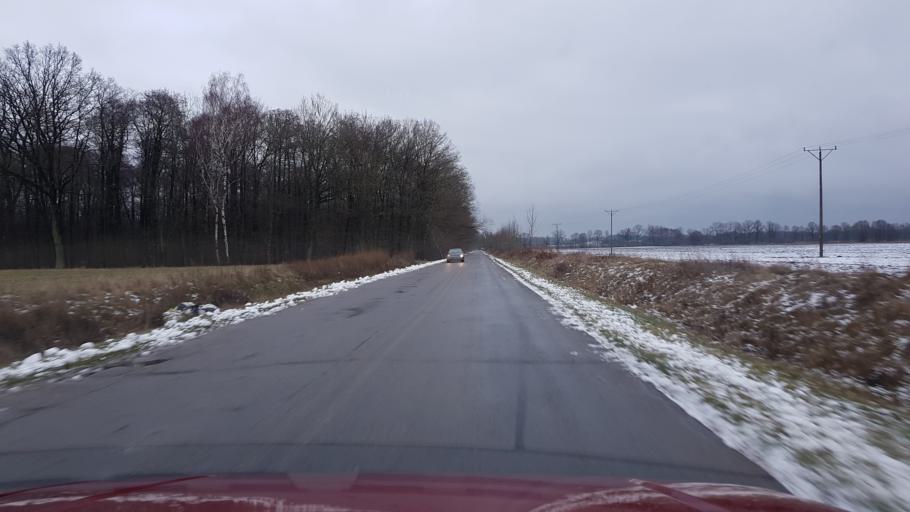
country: PL
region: West Pomeranian Voivodeship
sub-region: Powiat gryficki
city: Ploty
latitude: 53.8511
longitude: 15.3492
